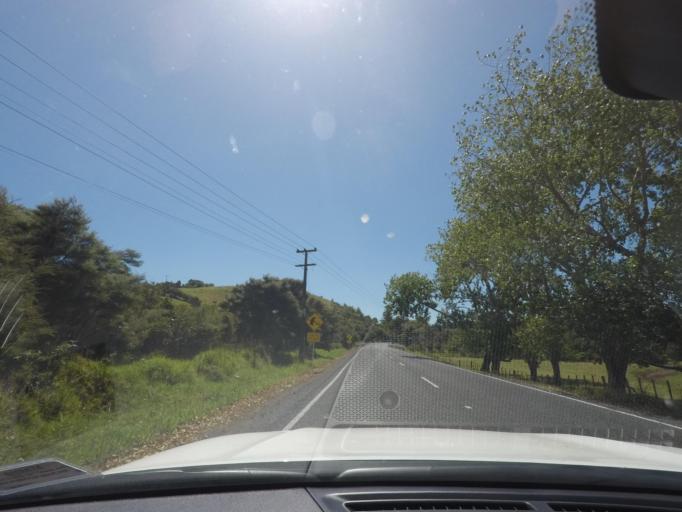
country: NZ
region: Auckland
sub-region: Auckland
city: Parakai
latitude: -36.5886
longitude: 174.3382
